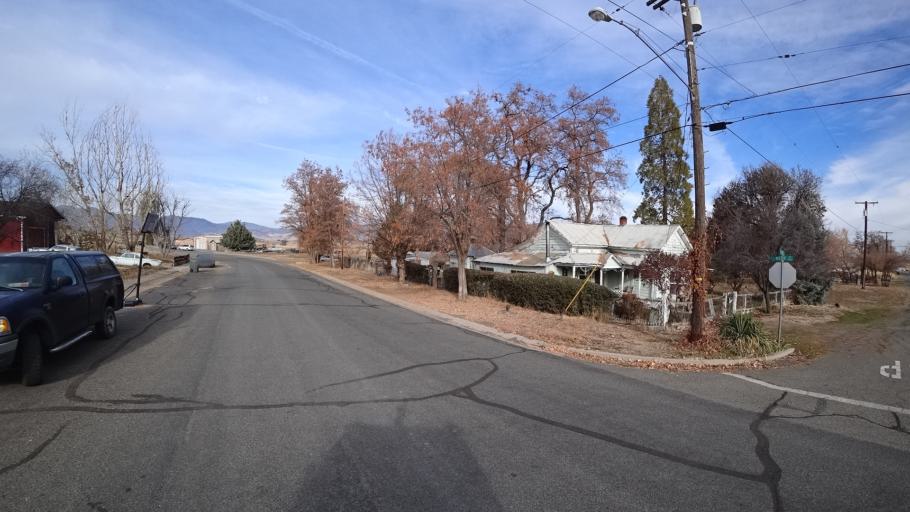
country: US
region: California
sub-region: Siskiyou County
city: Montague
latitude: 41.7308
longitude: -122.5341
